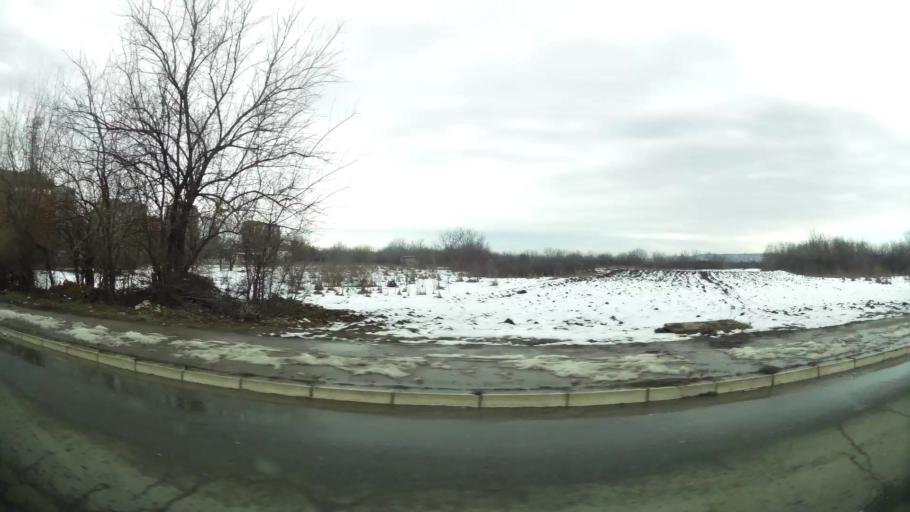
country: RS
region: Central Serbia
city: Sremcica
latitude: 44.7287
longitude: 20.3849
